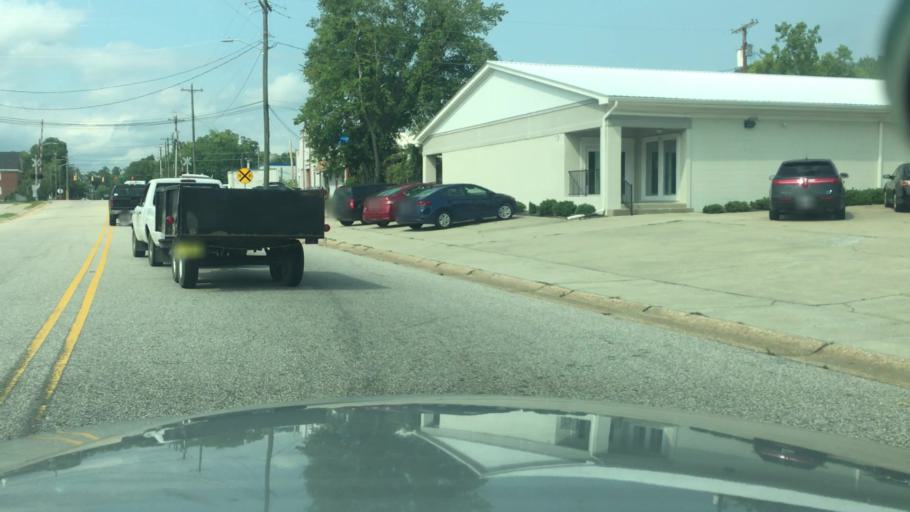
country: US
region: North Carolina
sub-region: Cumberland County
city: Fayetteville
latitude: 35.0454
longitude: -78.8614
